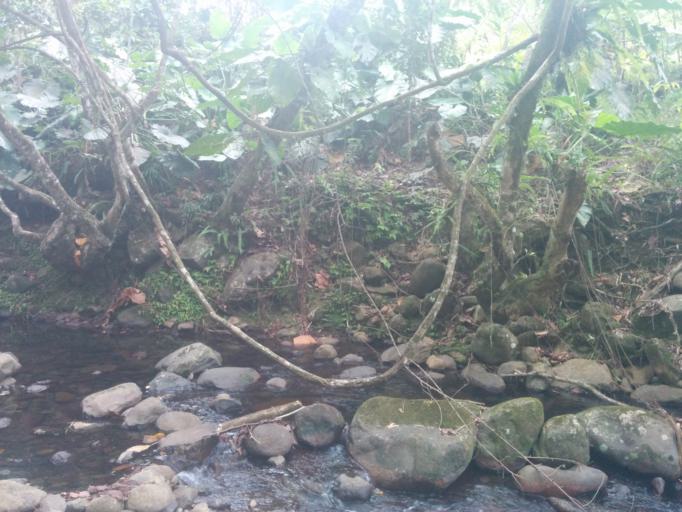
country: GP
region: Guadeloupe
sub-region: Guadeloupe
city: Capesterre-Belle-Eau
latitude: 16.1062
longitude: -61.6088
